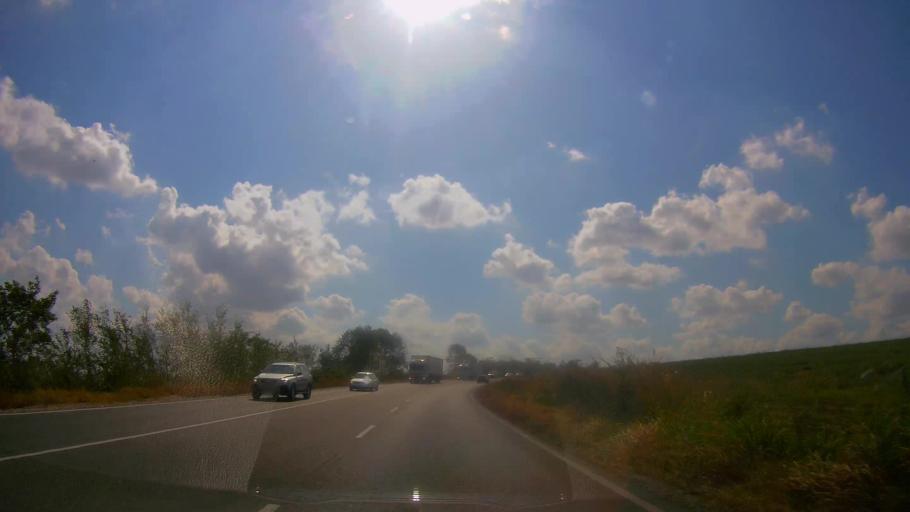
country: BG
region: Ruse
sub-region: Obshtina Ivanovo
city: Ivanovo
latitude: 43.7283
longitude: 25.9185
